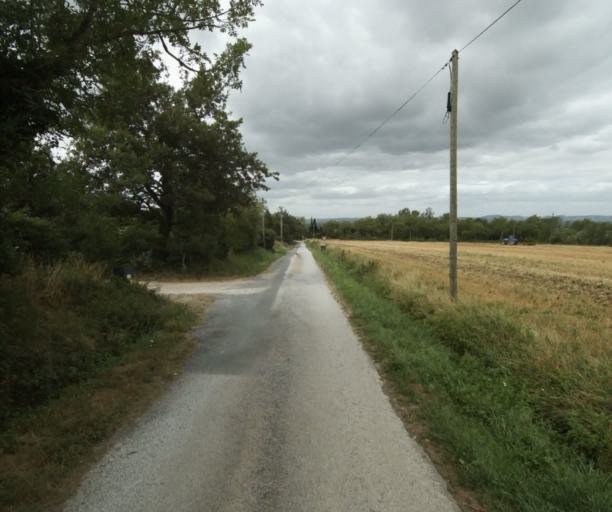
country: FR
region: Midi-Pyrenees
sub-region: Departement du Tarn
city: Soreze
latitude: 43.4567
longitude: 2.0791
